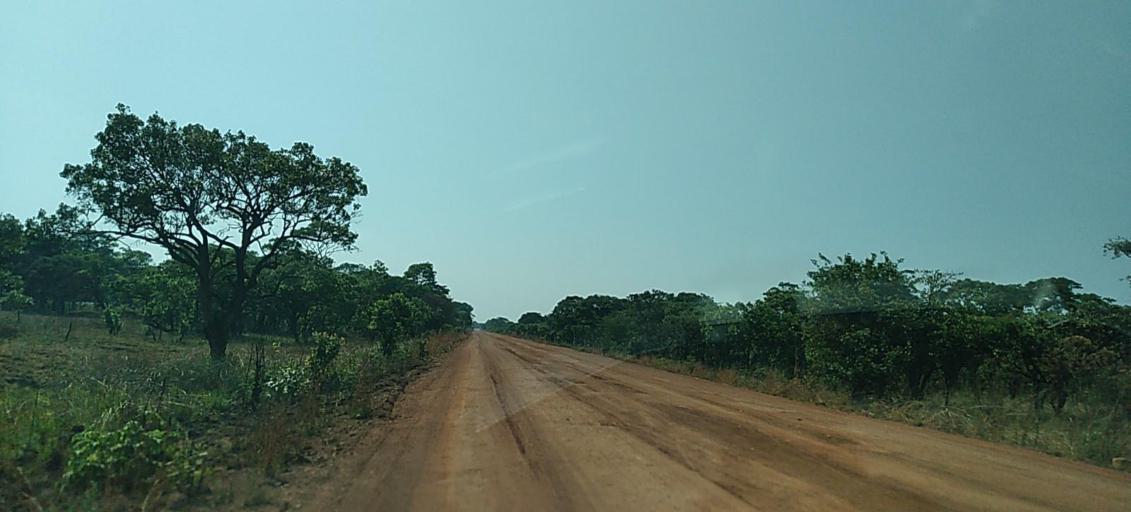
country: ZM
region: North-Western
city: Mwinilunga
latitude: -11.9127
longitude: 25.3017
